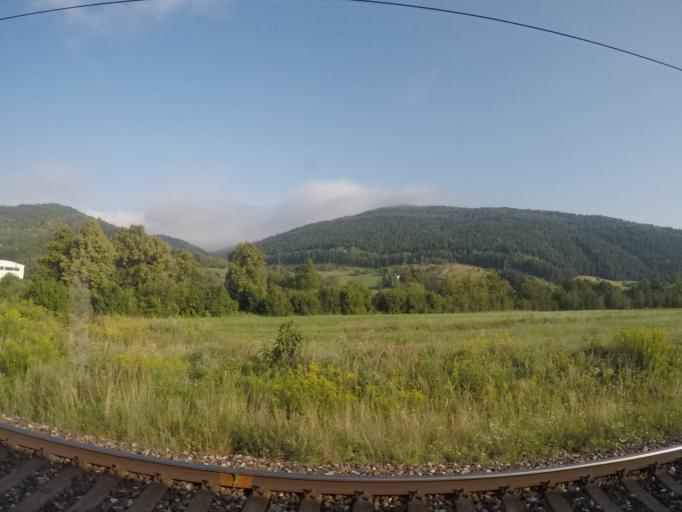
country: SK
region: Kosicky
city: Krompachy
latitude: 48.9251
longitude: 20.9040
